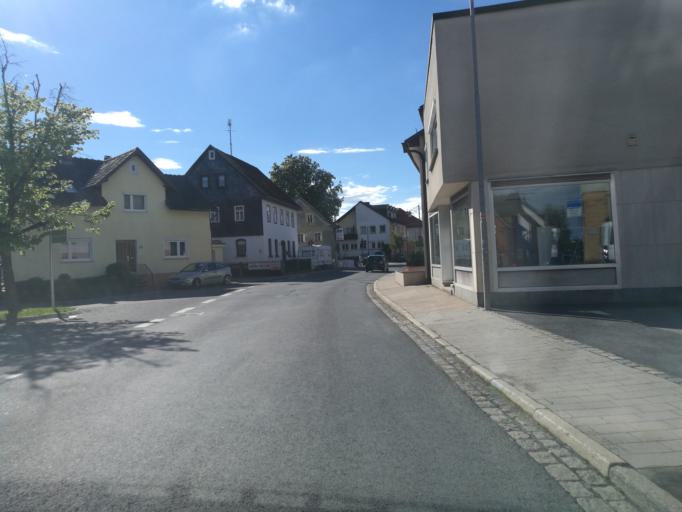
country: DE
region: Bavaria
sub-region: Upper Franconia
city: Sonnefeld
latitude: 50.2190
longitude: 11.0731
